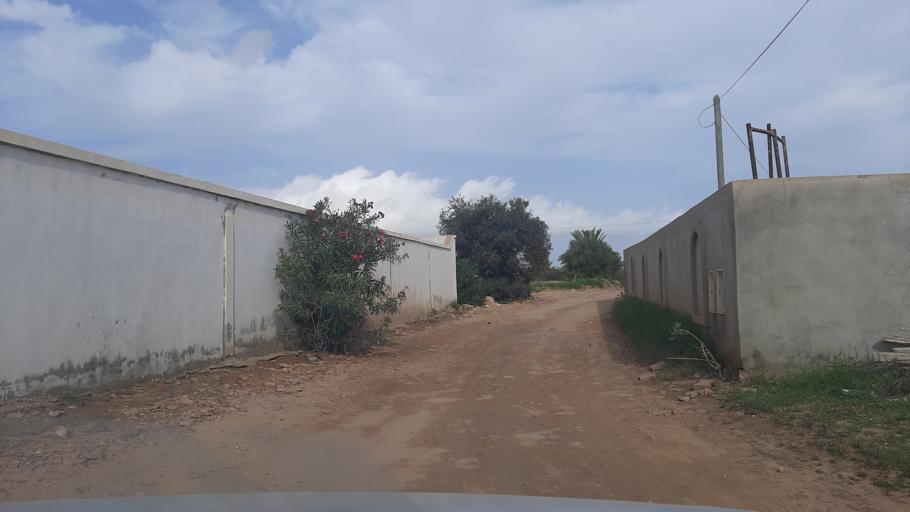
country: TN
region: Madanin
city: Midoun
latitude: 33.8069
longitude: 11.0238
